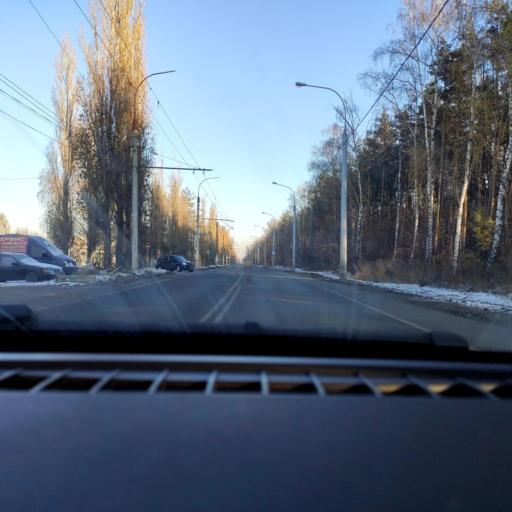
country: RU
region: Voronezj
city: Somovo
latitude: 51.7032
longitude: 39.2905
